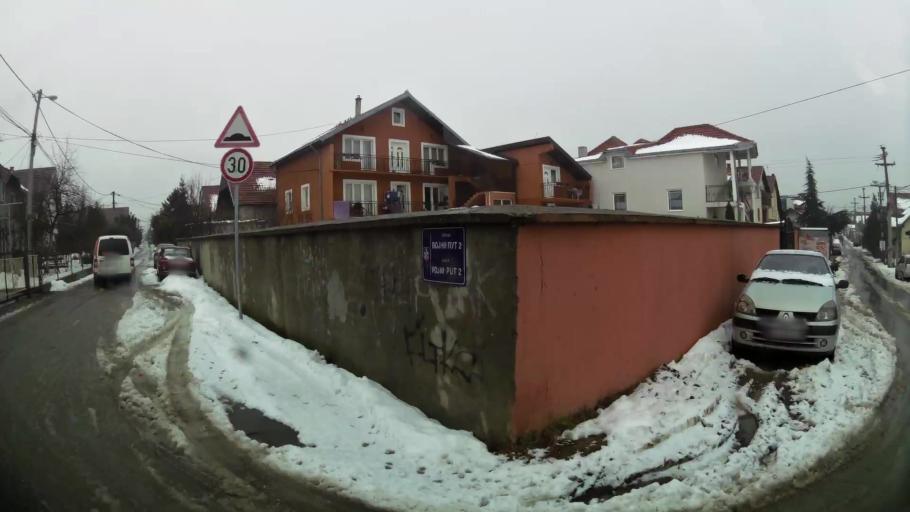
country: RS
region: Central Serbia
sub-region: Belgrade
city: Zemun
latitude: 44.8412
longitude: 20.3611
